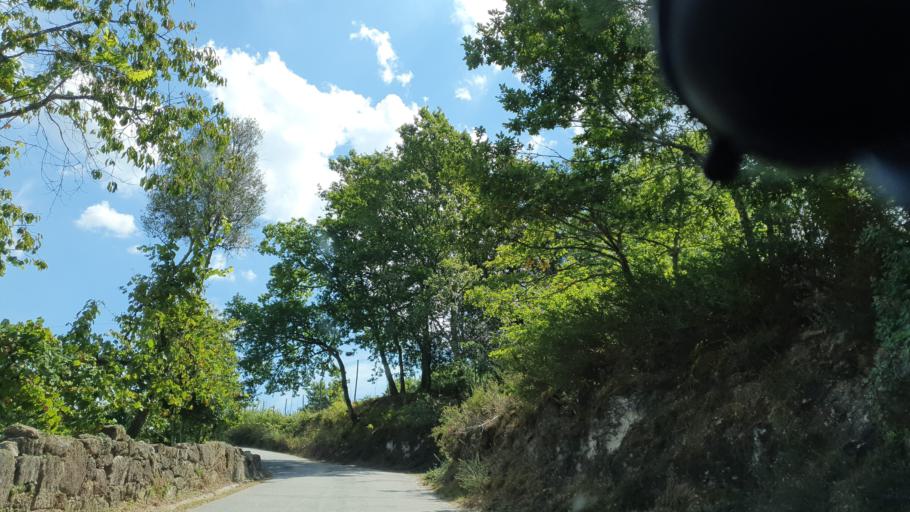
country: PT
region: Braga
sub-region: Vieira do Minho
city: Vieira do Minho
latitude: 41.7053
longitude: -8.0541
